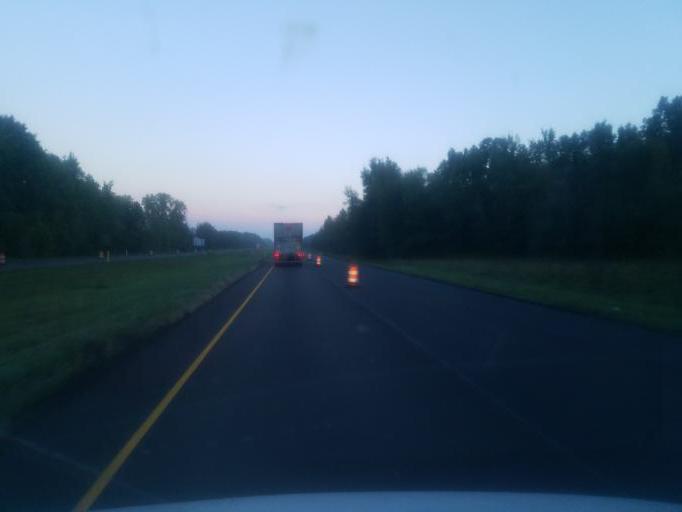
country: US
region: Ohio
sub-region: Ashtabula County
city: Jefferson
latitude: 41.7651
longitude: -80.7209
